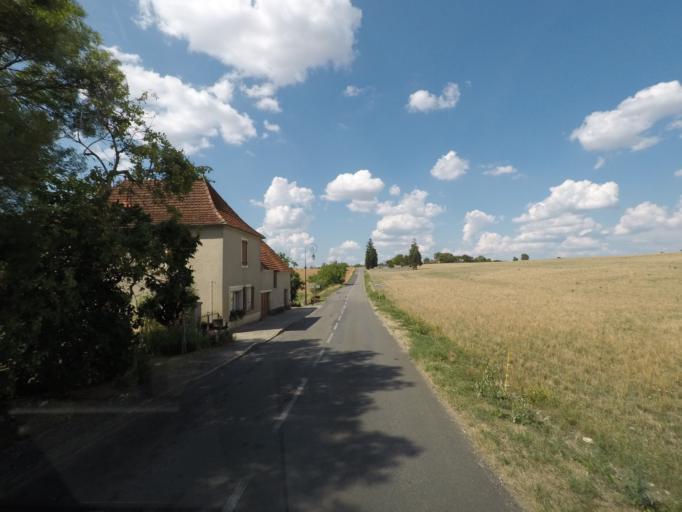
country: FR
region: Midi-Pyrenees
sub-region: Departement du Lot
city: Le Vigan
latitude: 44.6334
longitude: 1.5945
